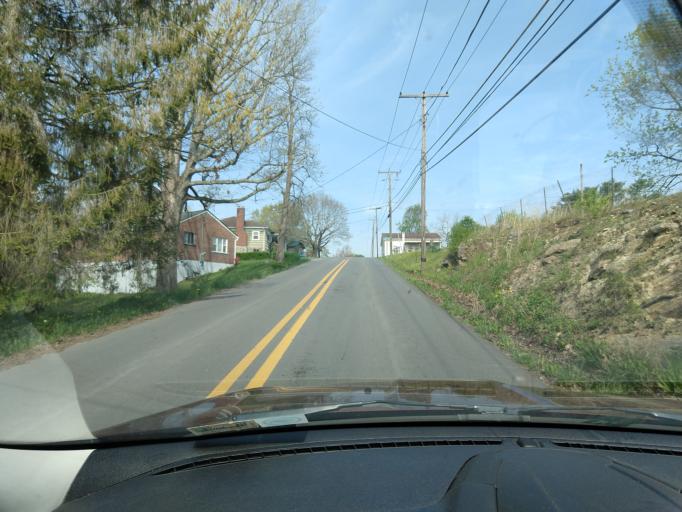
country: US
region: West Virginia
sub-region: Raleigh County
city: Crab Orchard
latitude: 37.7466
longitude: -81.2329
